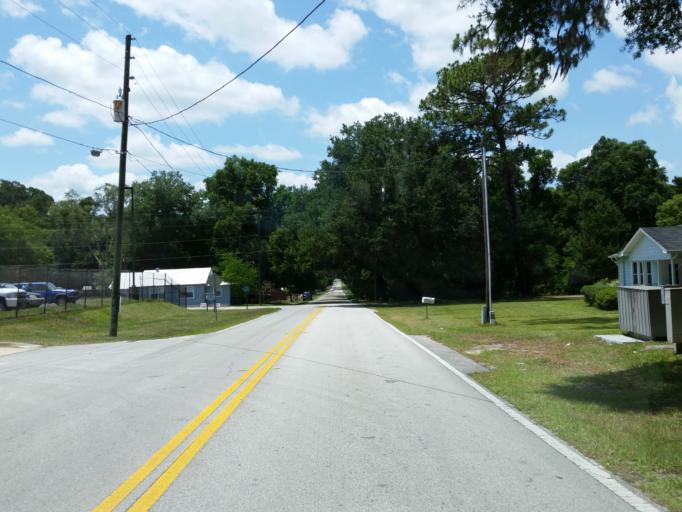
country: US
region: Florida
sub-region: Marion County
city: Belleview
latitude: 29.0113
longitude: -82.0424
